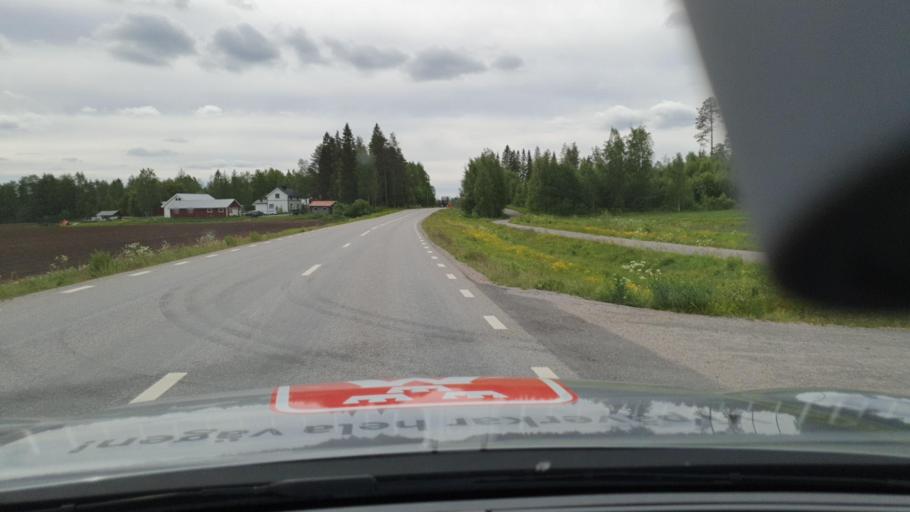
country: SE
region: Norrbotten
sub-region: Kalix Kommun
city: Kalix
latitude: 65.9283
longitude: 23.4616
